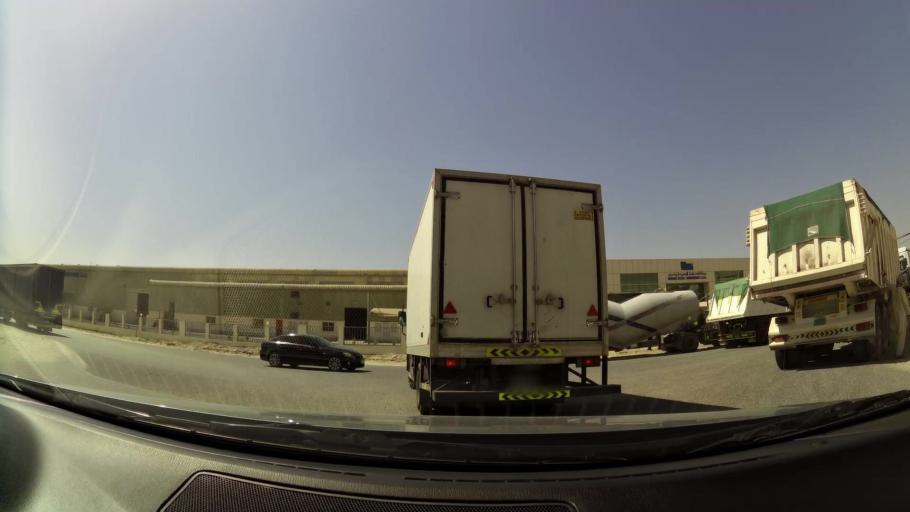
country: AE
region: Dubai
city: Dubai
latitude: 24.9725
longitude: 55.1742
